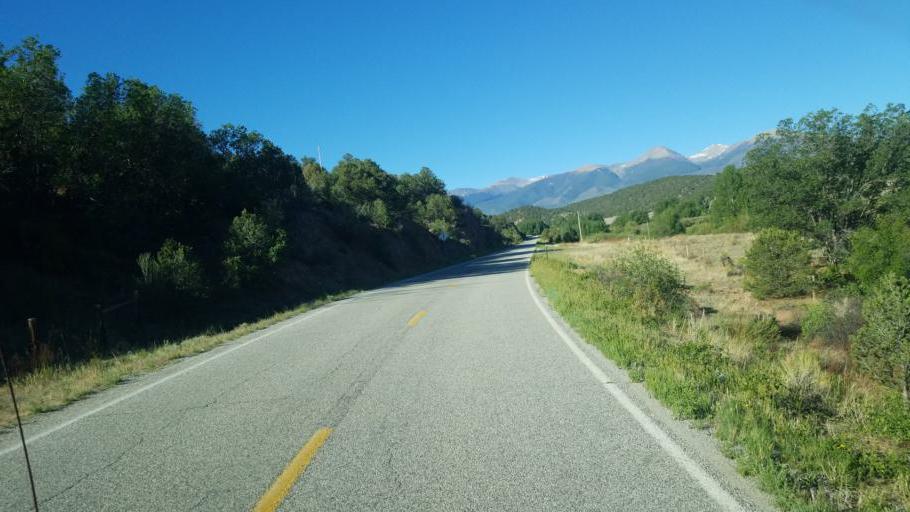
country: US
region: Colorado
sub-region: Custer County
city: Westcliffe
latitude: 38.3560
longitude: -105.5906
